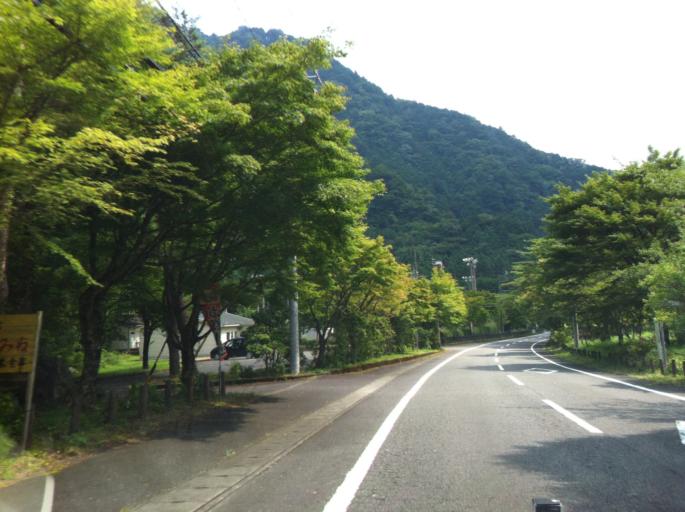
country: JP
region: Shizuoka
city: Fujinomiya
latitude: 35.2656
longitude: 138.3298
